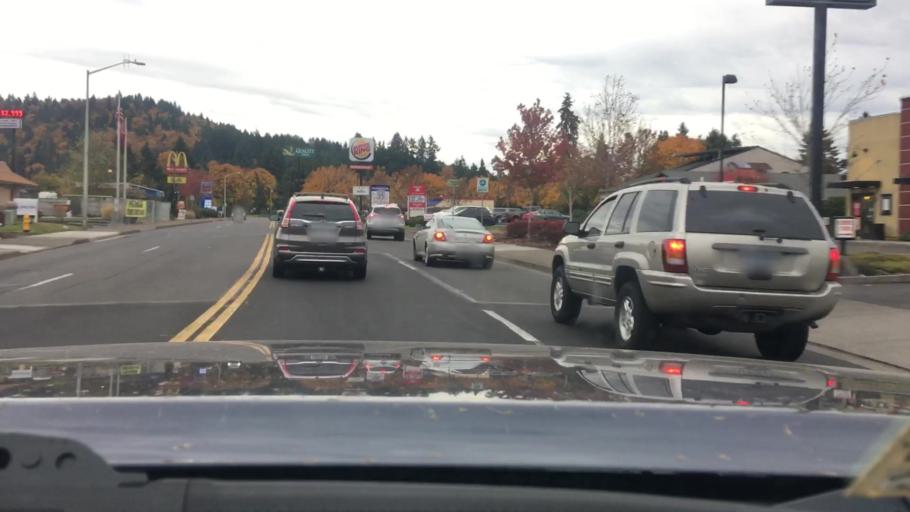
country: US
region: Oregon
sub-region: Lane County
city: Cottage Grove
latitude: 43.8042
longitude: -123.0454
